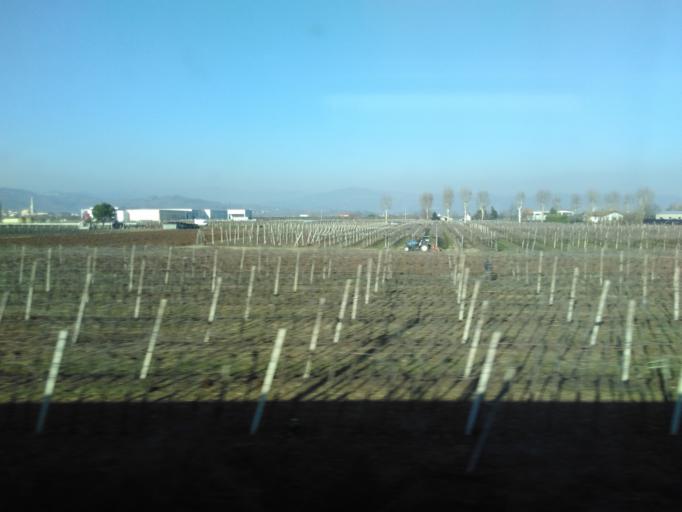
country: IT
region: Veneto
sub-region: Provincia di Verona
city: San Bonifacio
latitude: 45.4060
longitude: 11.3022
